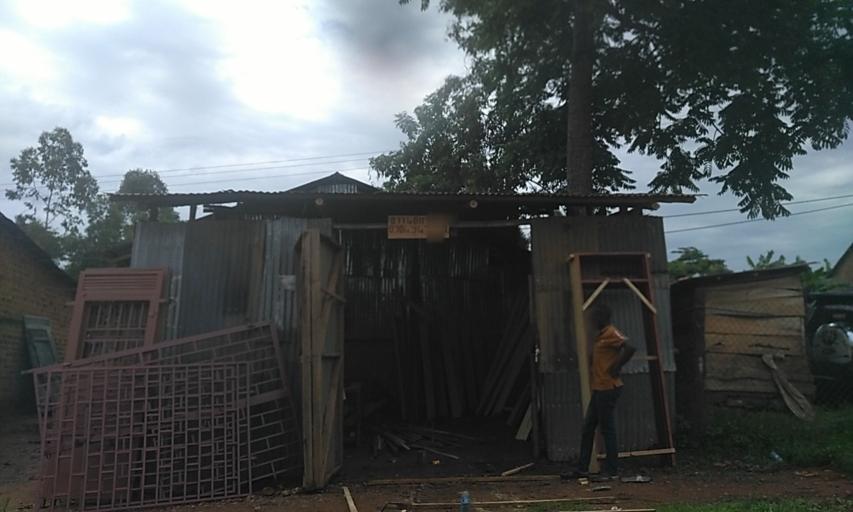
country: UG
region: Central Region
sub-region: Wakiso District
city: Bweyogerere
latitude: 0.3948
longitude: 32.6875
